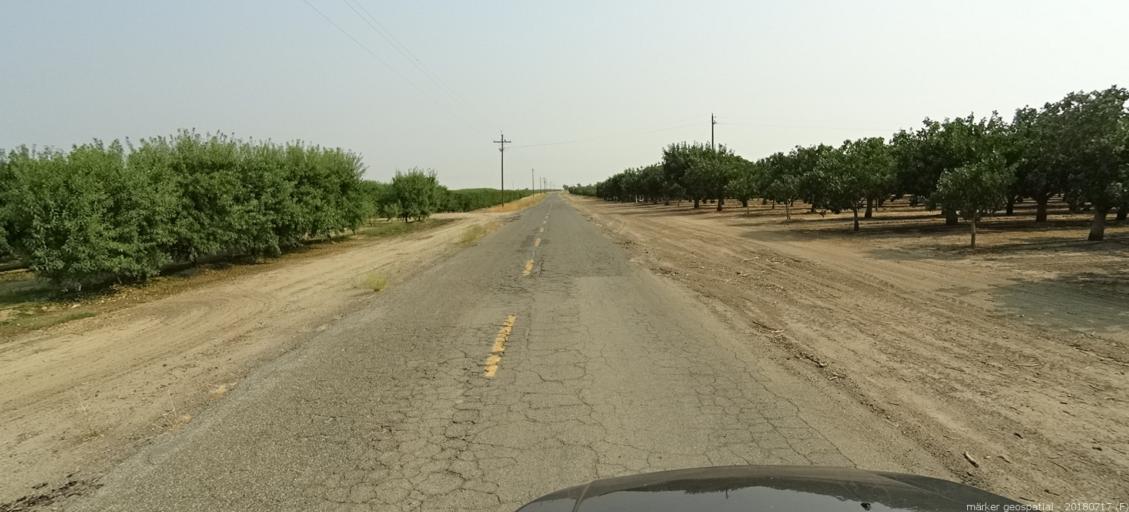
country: US
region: California
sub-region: Madera County
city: Fairmead
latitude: 37.1084
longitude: -120.1111
